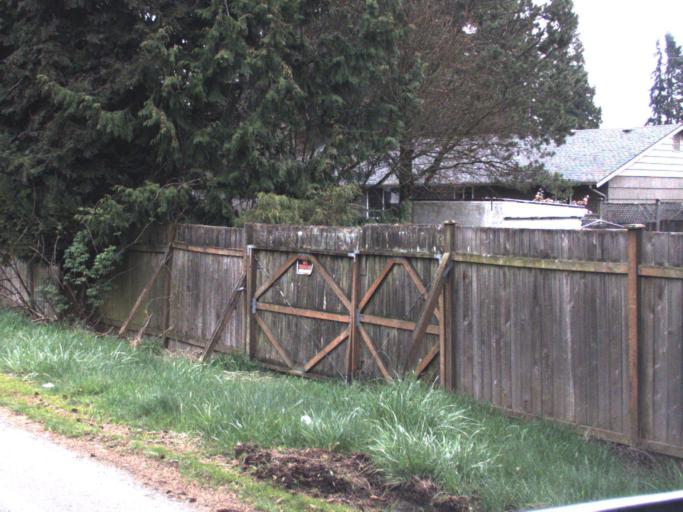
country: US
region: Washington
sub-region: King County
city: Federal Way
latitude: 47.3317
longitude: -122.3427
